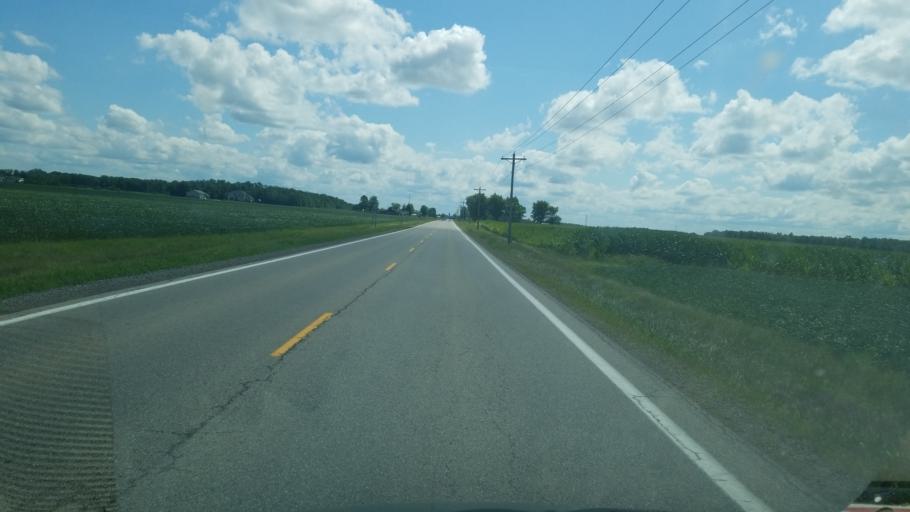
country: US
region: Ohio
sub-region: Putnam County
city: Kalida
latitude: 41.0266
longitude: -84.1981
